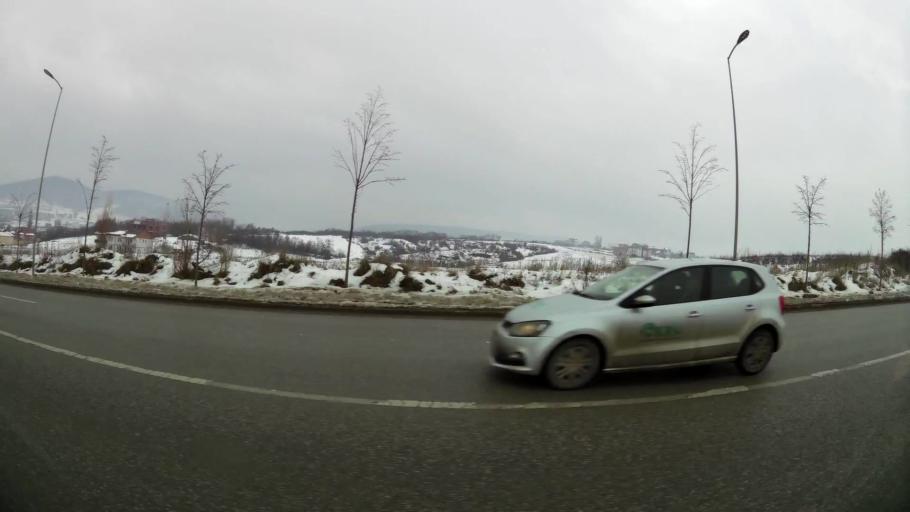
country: XK
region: Pristina
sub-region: Komuna e Prishtines
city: Pristina
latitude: 42.7051
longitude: 21.1556
